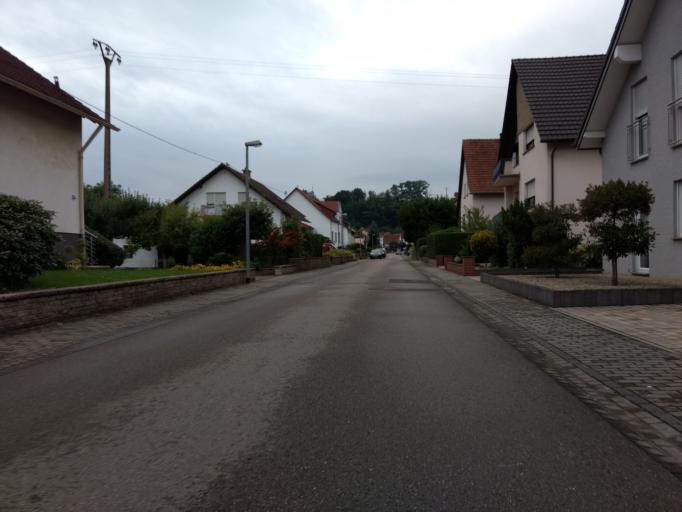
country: DE
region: Saarland
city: Nalbach
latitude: 49.3701
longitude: 6.7684
